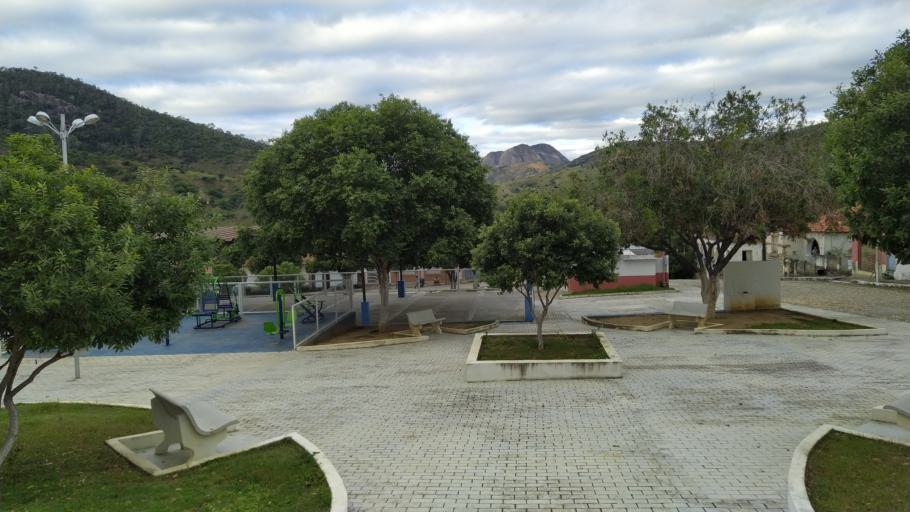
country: BR
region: Minas Gerais
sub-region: Almenara
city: Almenara
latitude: -16.5195
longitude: -40.4437
